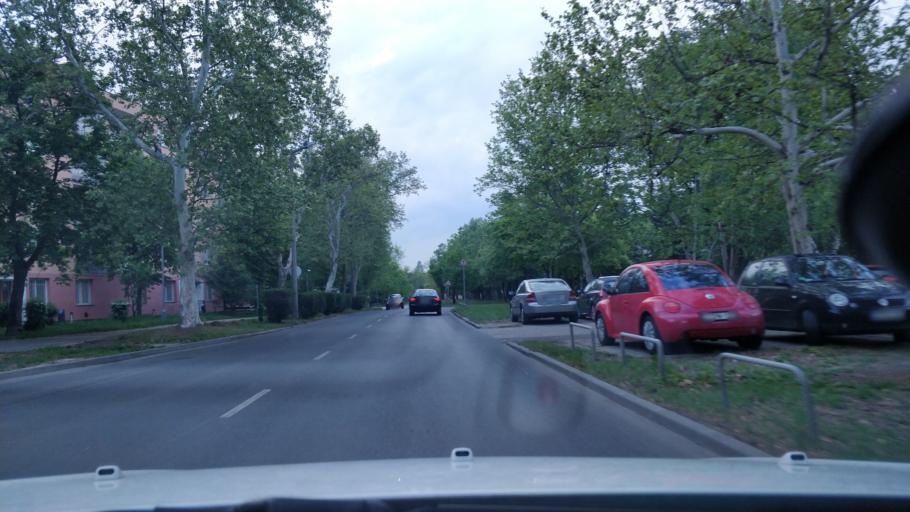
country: HU
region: Bacs-Kiskun
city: Kecskemet
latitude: 46.9103
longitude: 19.6760
